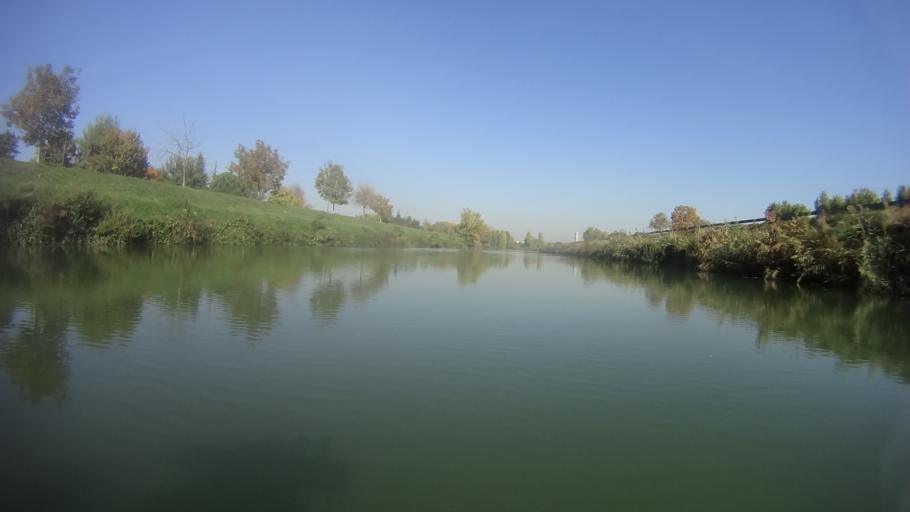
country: IT
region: Veneto
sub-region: Provincia di Padova
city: Padova
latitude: 45.3961
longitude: 11.9132
